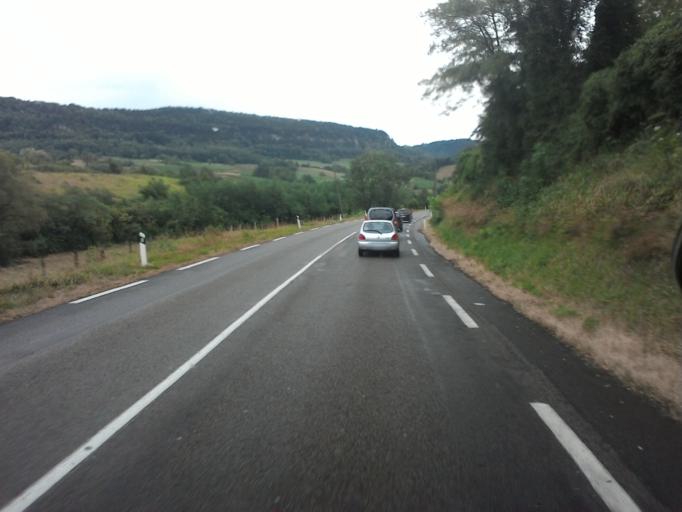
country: FR
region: Franche-Comte
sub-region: Departement du Jura
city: Poligny
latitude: 46.8570
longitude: 5.7125
